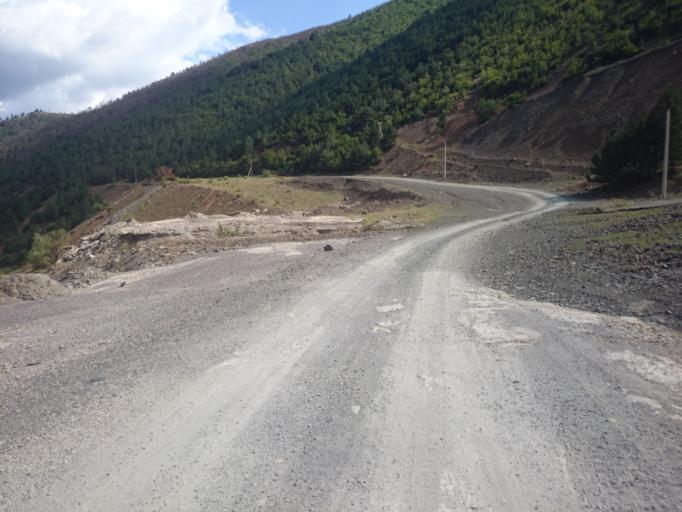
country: AL
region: Lezhe
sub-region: Rrethi i Lezhes
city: Blinisht
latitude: 41.8695
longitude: 20.0332
